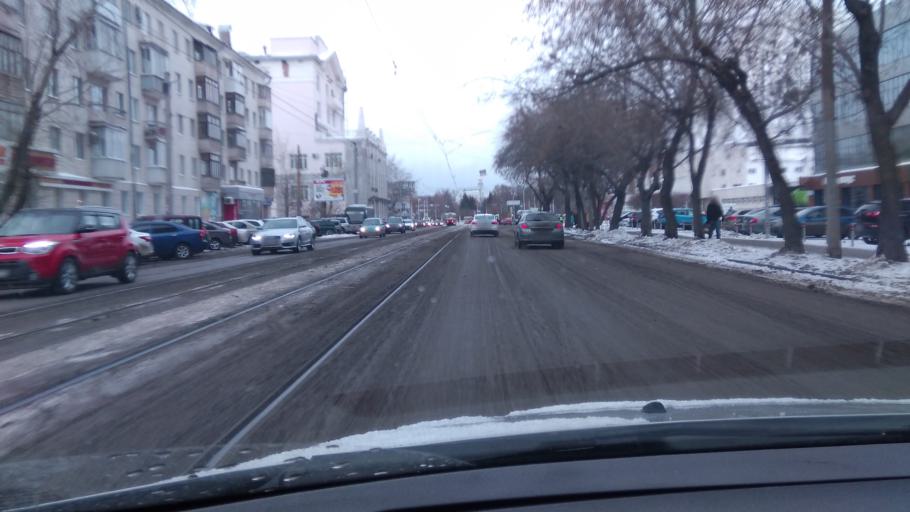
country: RU
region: Sverdlovsk
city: Yekaterinburg
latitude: 56.8239
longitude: 60.6044
